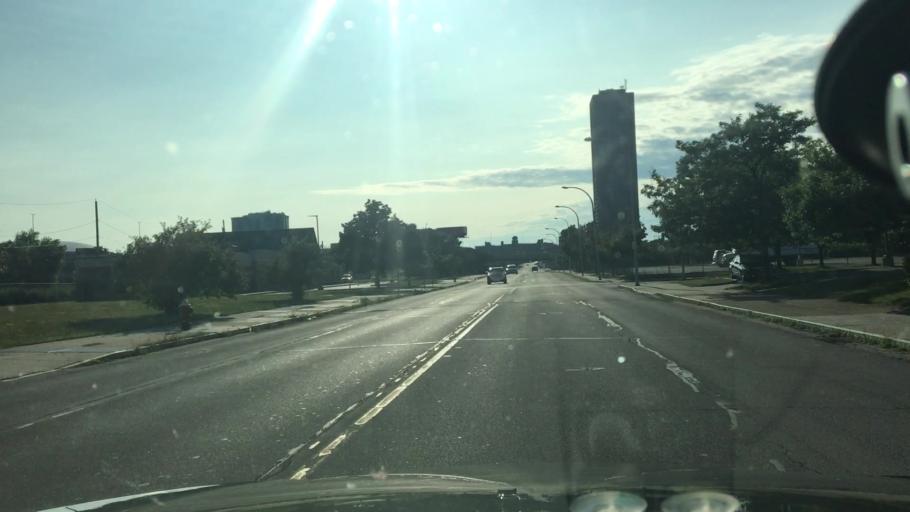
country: US
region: New York
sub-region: Erie County
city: Buffalo
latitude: 42.8773
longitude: -78.8657
